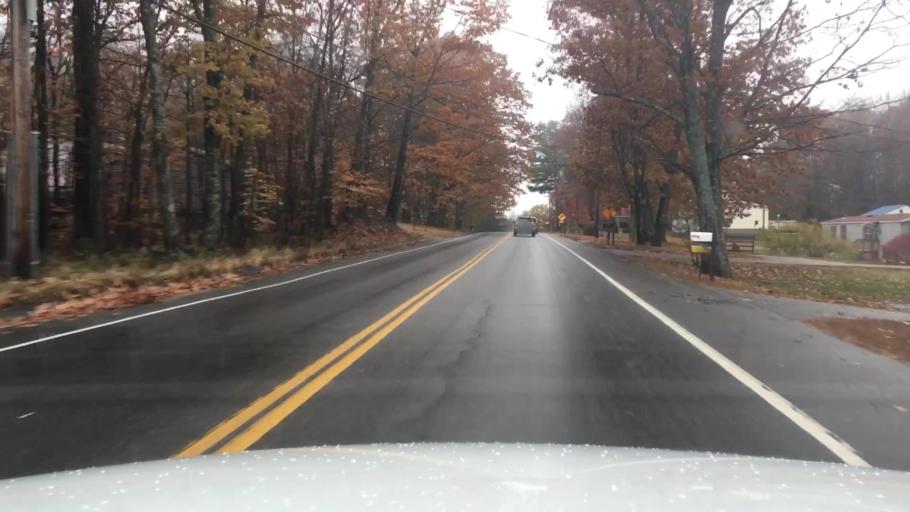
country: US
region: Maine
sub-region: Androscoggin County
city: Sabattus
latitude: 44.1134
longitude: -70.0982
